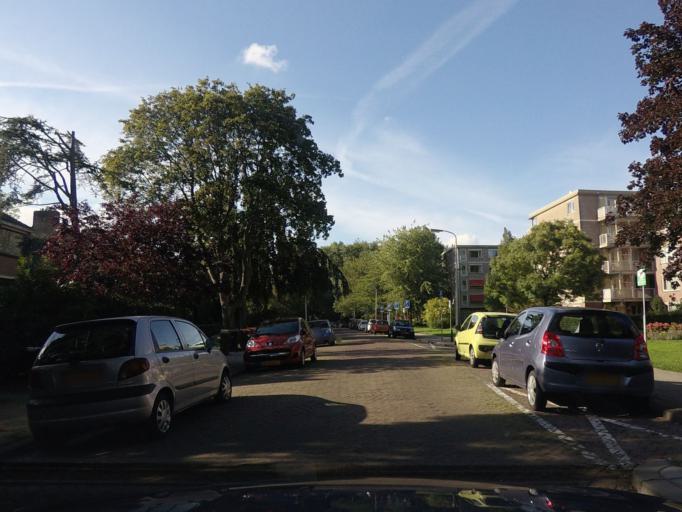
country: NL
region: South Holland
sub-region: Gemeente Leidschendam-Voorburg
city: Voorburg
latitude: 52.0993
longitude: 4.3641
